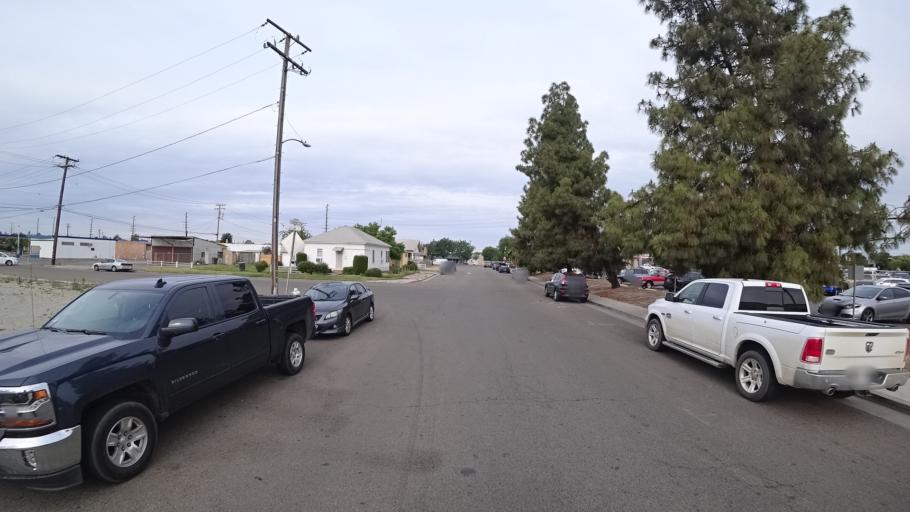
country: US
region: California
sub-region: Kings County
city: Hanford
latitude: 36.3264
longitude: -119.6537
